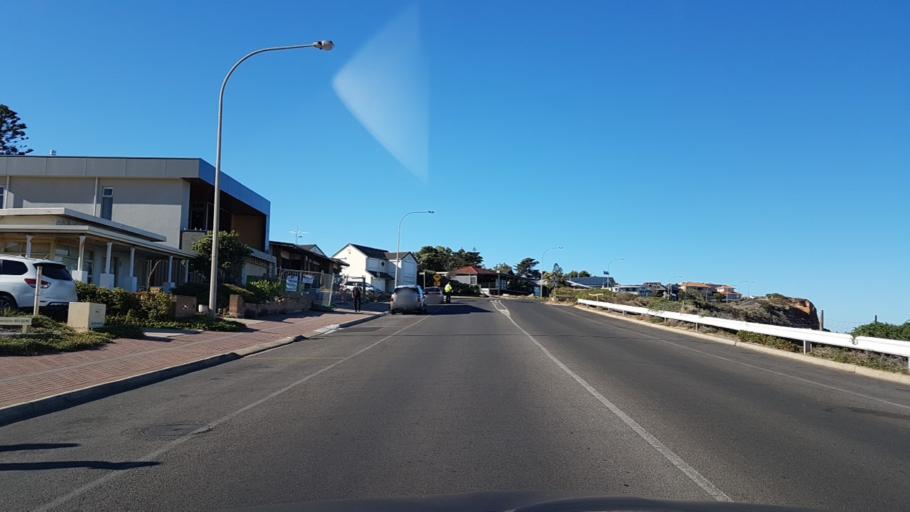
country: AU
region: South Australia
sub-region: Adelaide
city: Port Noarlunga
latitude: -35.1404
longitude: 138.4703
